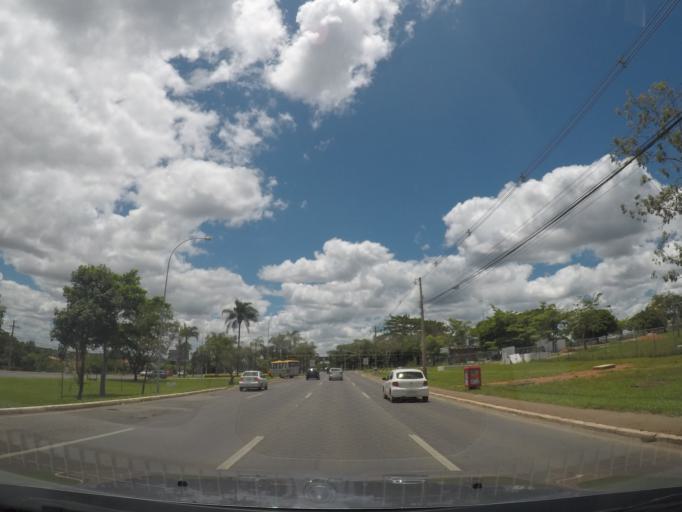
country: BR
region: Federal District
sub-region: Brasilia
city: Brasilia
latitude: -15.7222
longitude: -47.8878
